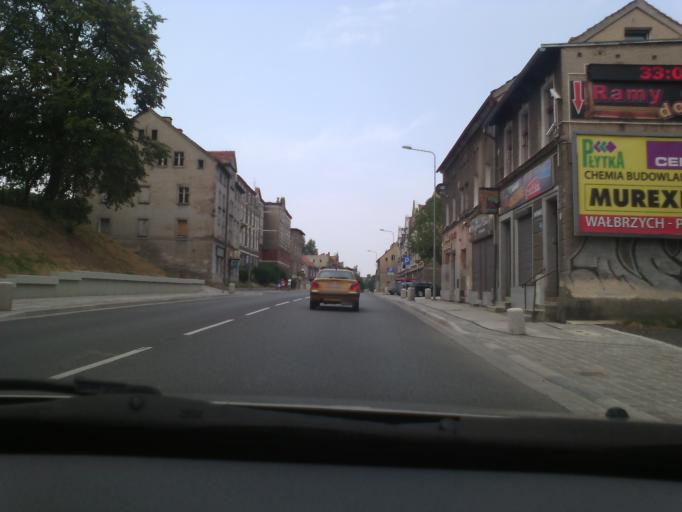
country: PL
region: Lower Silesian Voivodeship
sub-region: Powiat walbrzyski
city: Walbrzych
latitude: 50.7869
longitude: 16.2871
